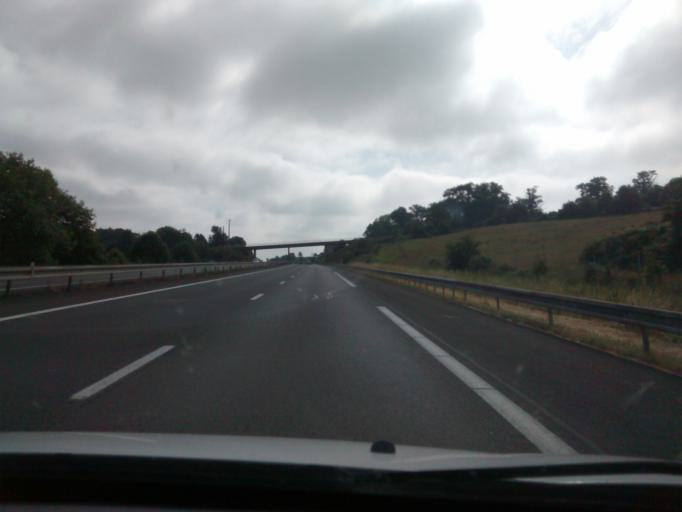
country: FR
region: Pays de la Loire
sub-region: Departement de la Sarthe
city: Coulans-sur-Gee
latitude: 48.0231
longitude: -0.0271
